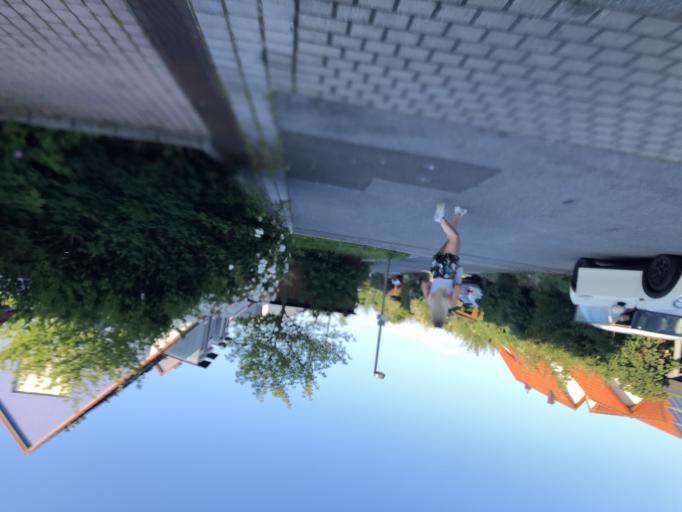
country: DE
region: Bavaria
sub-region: Regierungsbezirk Mittelfranken
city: Hessdorf
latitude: 49.5981
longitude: 10.9534
